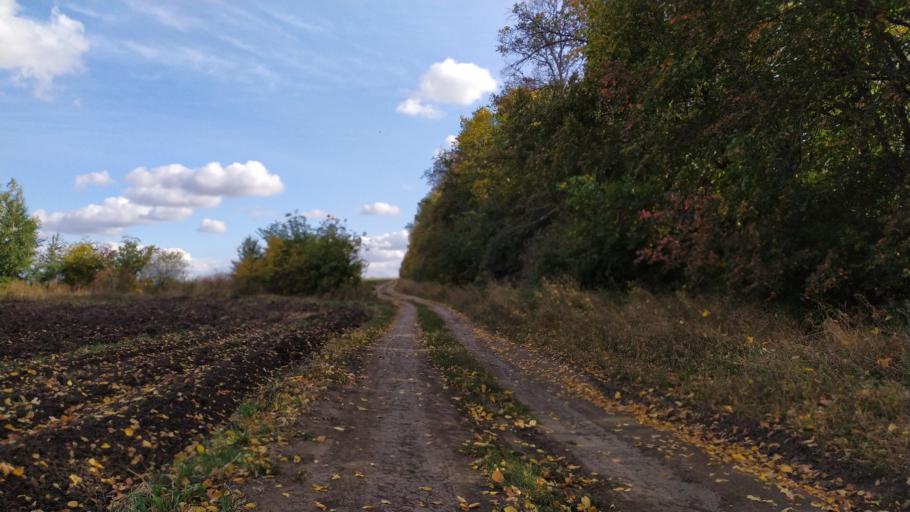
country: RU
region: Kursk
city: Kursk
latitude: 51.6224
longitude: 36.1614
